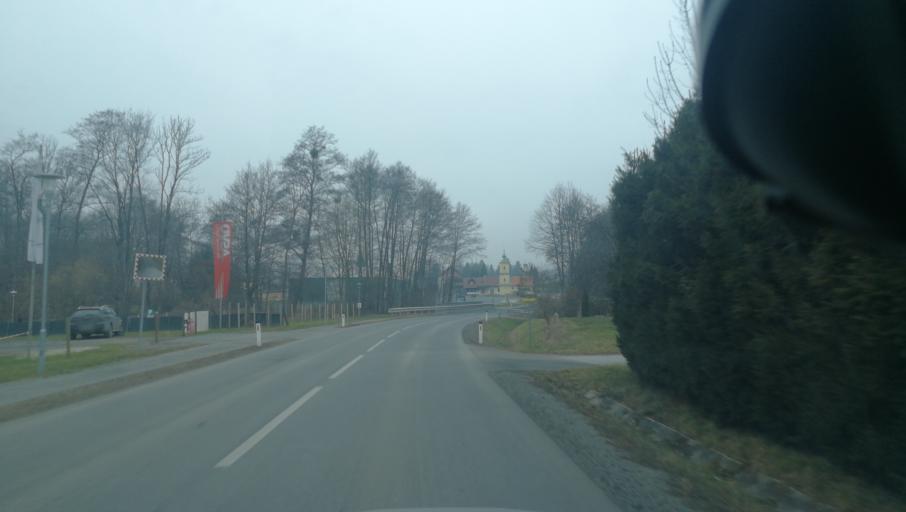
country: AT
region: Styria
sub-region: Politischer Bezirk Deutschlandsberg
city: Stainz
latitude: 46.9009
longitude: 15.2469
